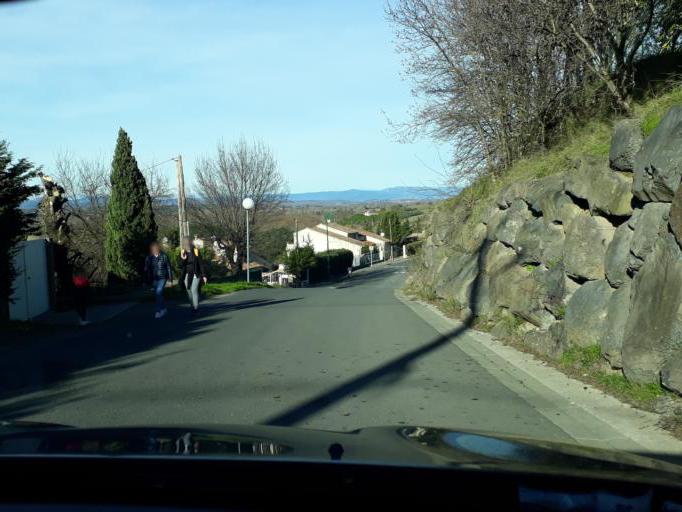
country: FR
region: Languedoc-Roussillon
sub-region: Departement de l'Herault
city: Castelnau-de-Guers
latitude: 43.4370
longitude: 3.4408
